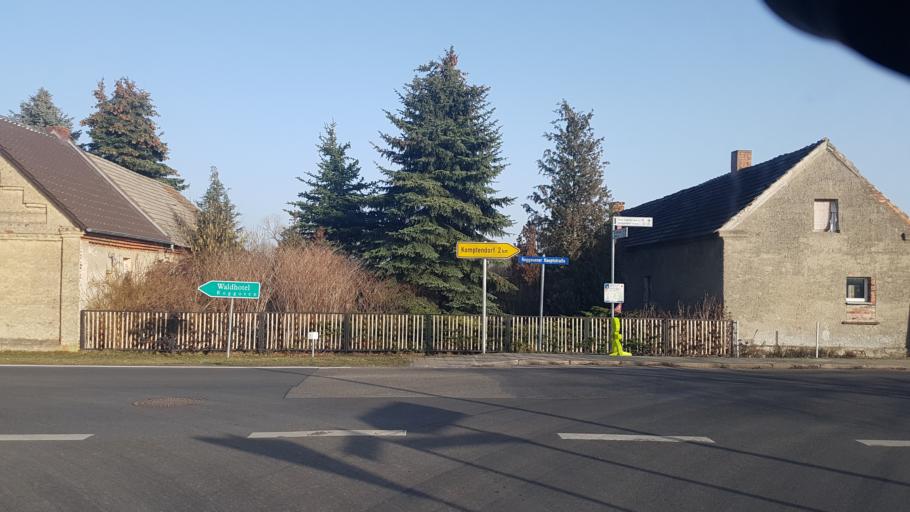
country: DE
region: Brandenburg
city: Heinersbruck
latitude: 51.7019
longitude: 14.4622
